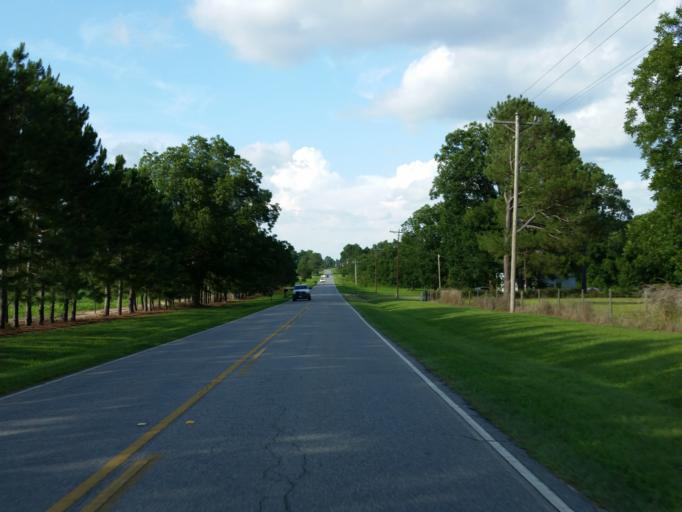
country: US
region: Georgia
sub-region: Crisp County
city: Cordele
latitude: 31.9973
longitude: -83.8631
